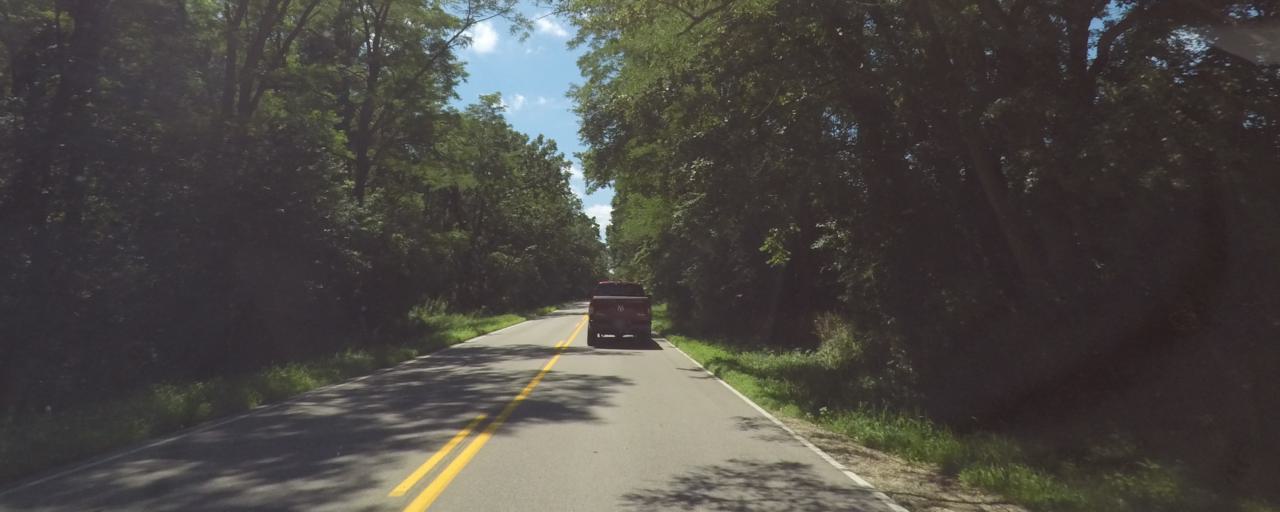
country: US
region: Wisconsin
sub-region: Waukesha County
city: Eagle
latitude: 42.9292
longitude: -88.5140
